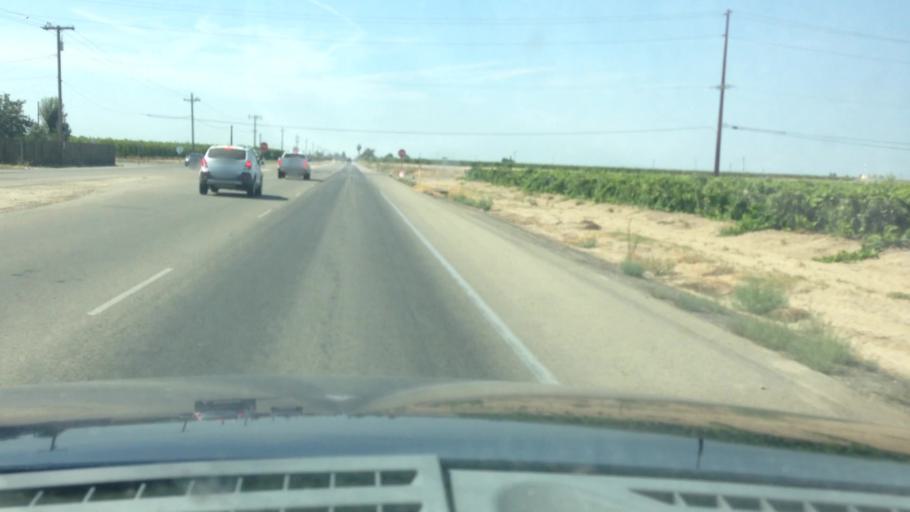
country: US
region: California
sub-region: Fresno County
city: Parlier
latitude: 36.6352
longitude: -119.5568
